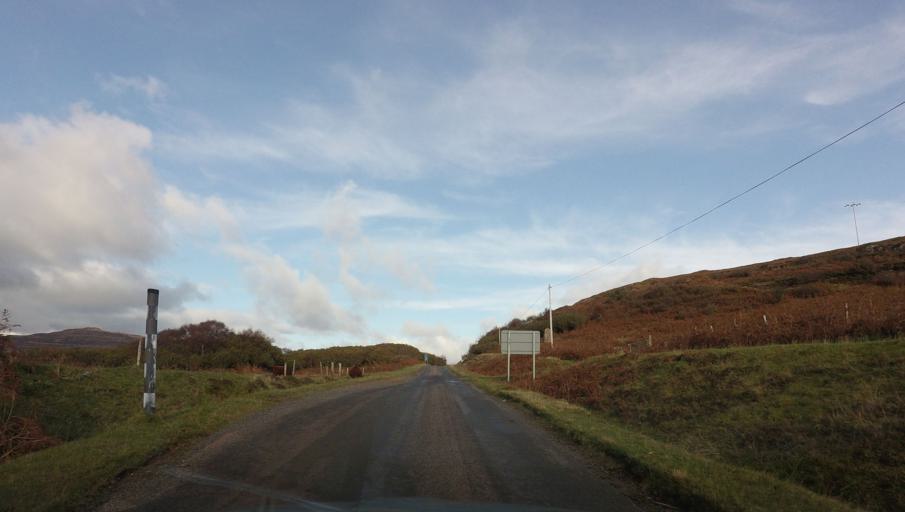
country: GB
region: Scotland
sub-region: Argyll and Bute
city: Isle Of Mull
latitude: 56.3289
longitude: -6.1985
